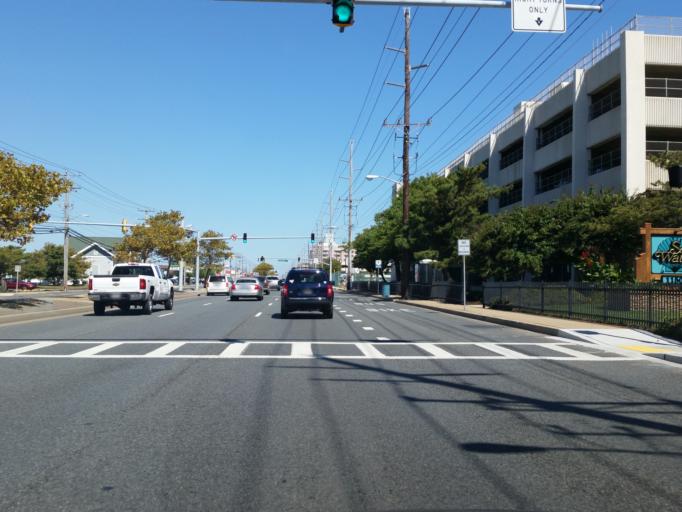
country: US
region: Maryland
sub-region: Worcester County
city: Ocean City
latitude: 38.4200
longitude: -75.0566
